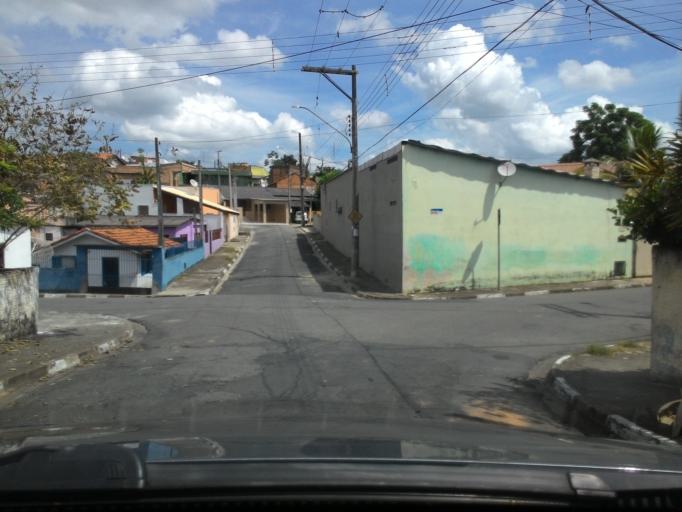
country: BR
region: Sao Paulo
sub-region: Registro
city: Registro
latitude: -24.4944
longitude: -47.8358
